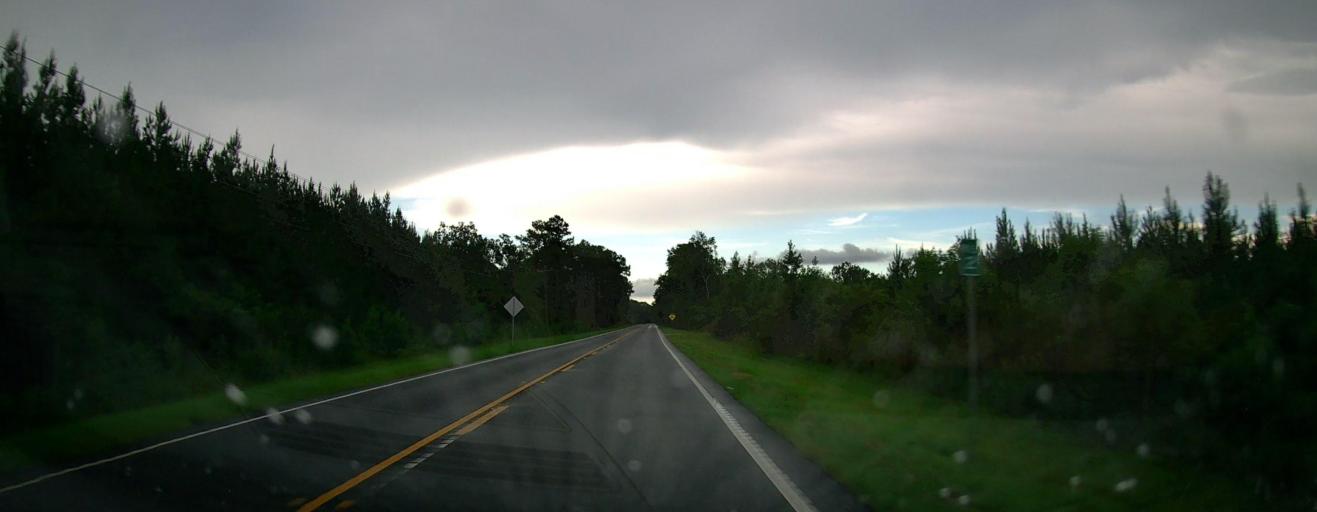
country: US
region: Georgia
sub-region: Glynn County
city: Dock Junction
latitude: 31.2988
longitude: -81.7032
